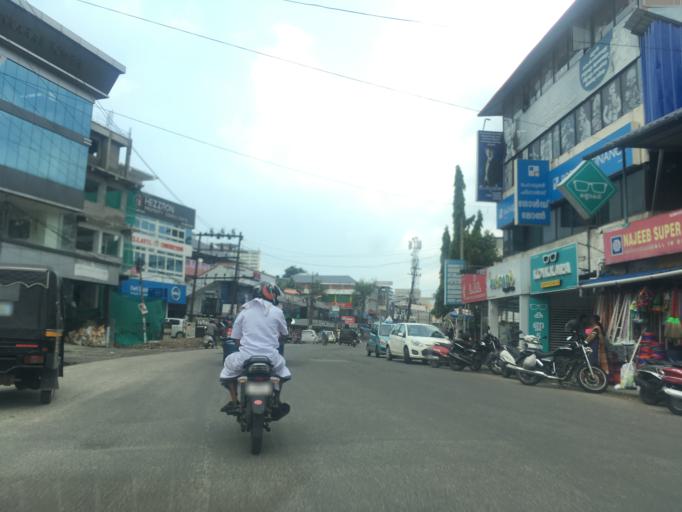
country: IN
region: Kerala
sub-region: Ernakulam
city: Elur
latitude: 10.0262
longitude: 76.3122
